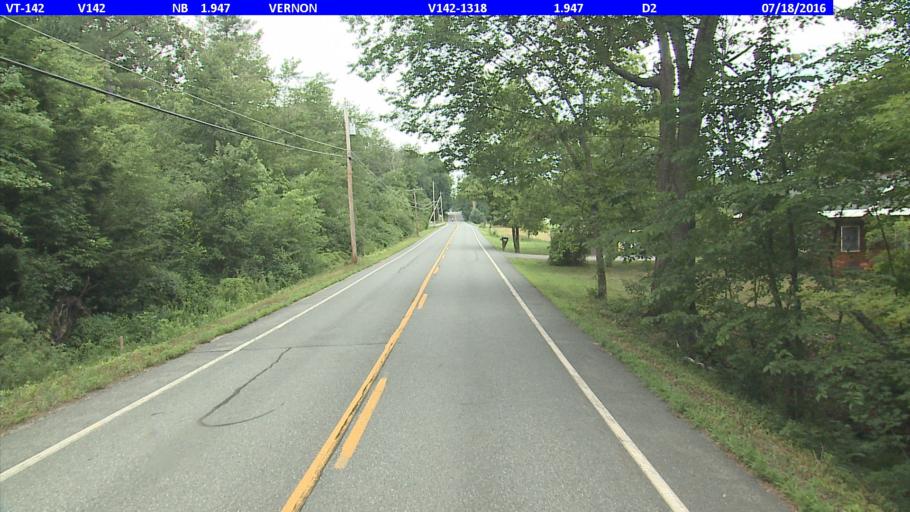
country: US
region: New Hampshire
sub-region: Cheshire County
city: Hinsdale
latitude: 42.7519
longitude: -72.4806
